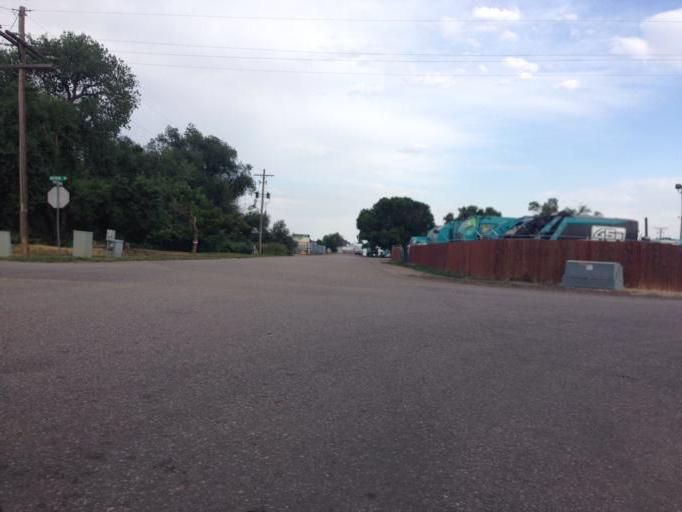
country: US
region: Colorado
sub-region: Larimer County
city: Fort Collins
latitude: 40.5845
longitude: -105.0426
